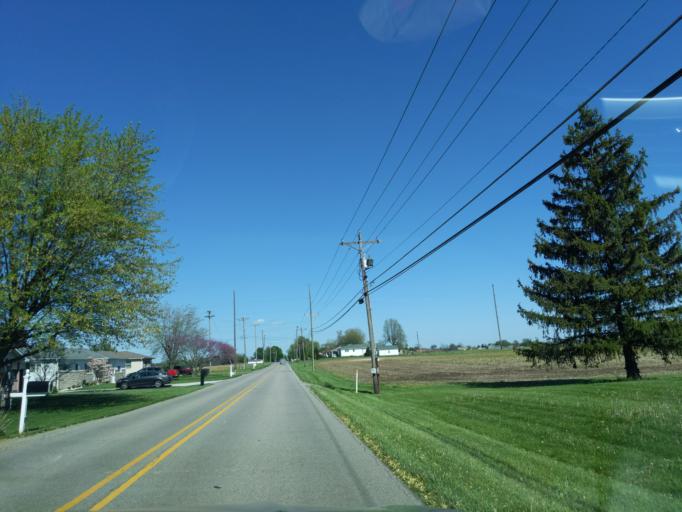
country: US
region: Indiana
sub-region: Decatur County
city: Greensburg
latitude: 39.3291
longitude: -85.5007
